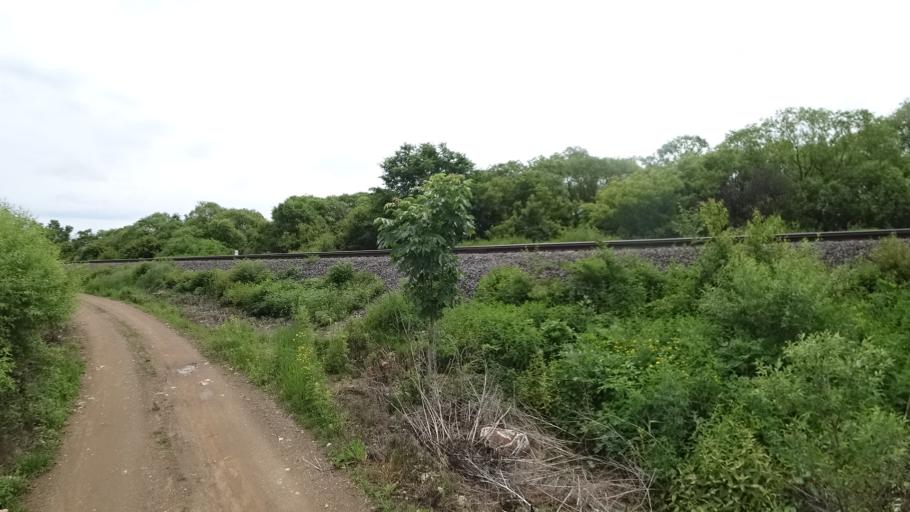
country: RU
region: Primorskiy
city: Novosysoyevka
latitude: 44.2482
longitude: 133.3721
